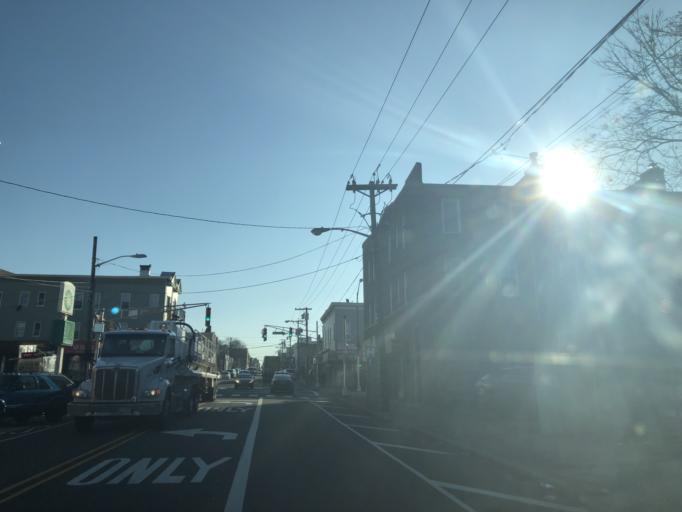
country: US
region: New Jersey
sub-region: Hudson County
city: Jersey City
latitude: 40.7210
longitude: -74.0820
